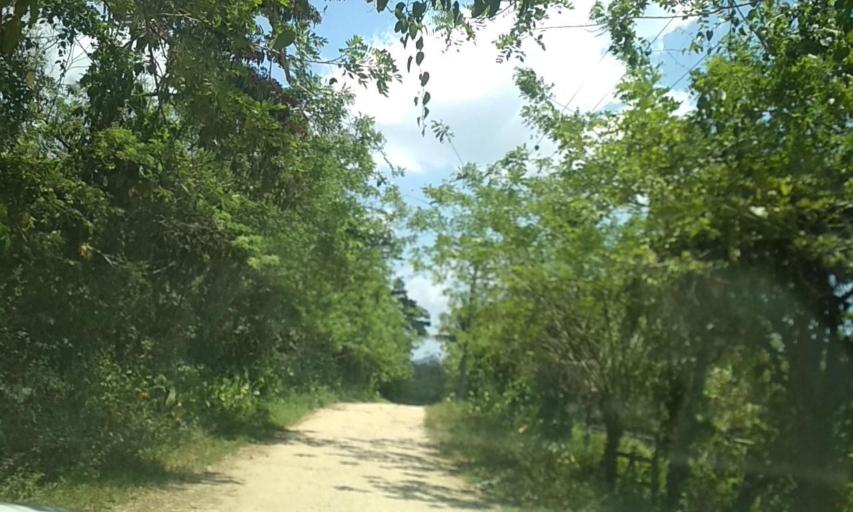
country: MX
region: Chiapas
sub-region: Tecpatan
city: Raudales Malpaso
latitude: 17.2888
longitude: -93.8417
